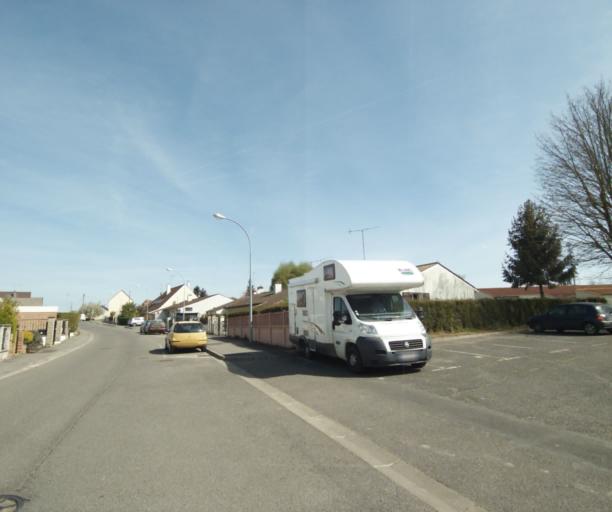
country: FR
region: Ile-de-France
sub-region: Departement de Seine-et-Marne
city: Nangis
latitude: 48.5533
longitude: 3.0231
